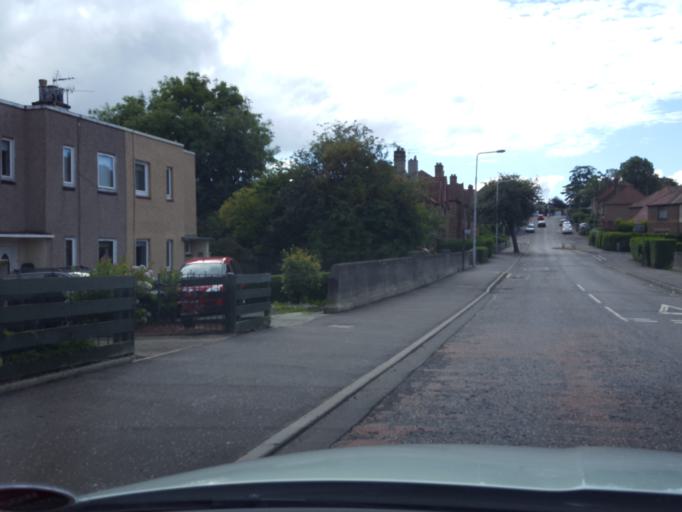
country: GB
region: Scotland
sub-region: Fife
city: Townhill
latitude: 56.0635
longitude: -3.4360
